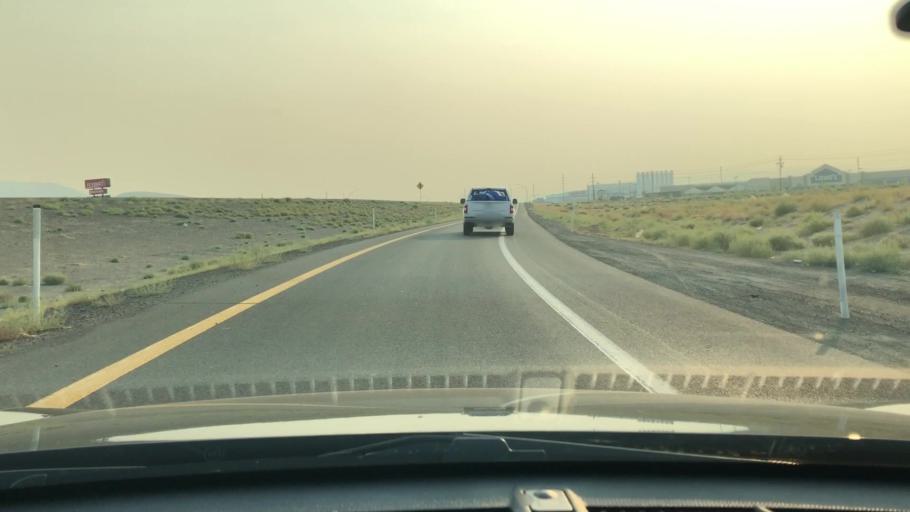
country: US
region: Nevada
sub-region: Lyon County
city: Fernley
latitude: 39.6125
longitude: -119.2175
